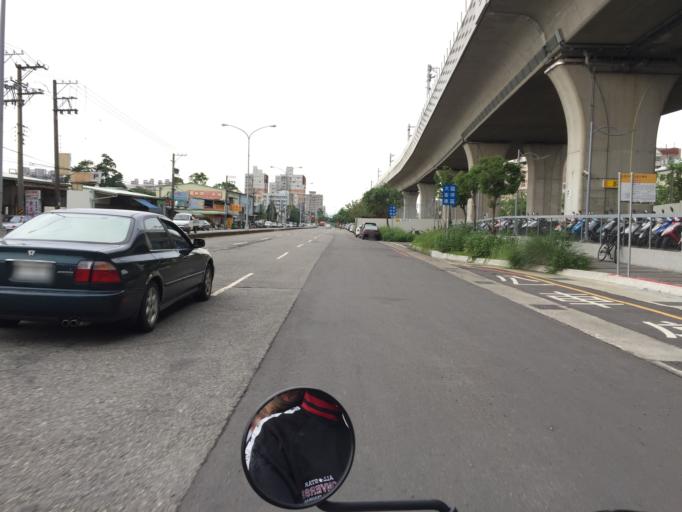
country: TW
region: Taiwan
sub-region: Taichung City
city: Taichung
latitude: 24.1636
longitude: 120.6999
